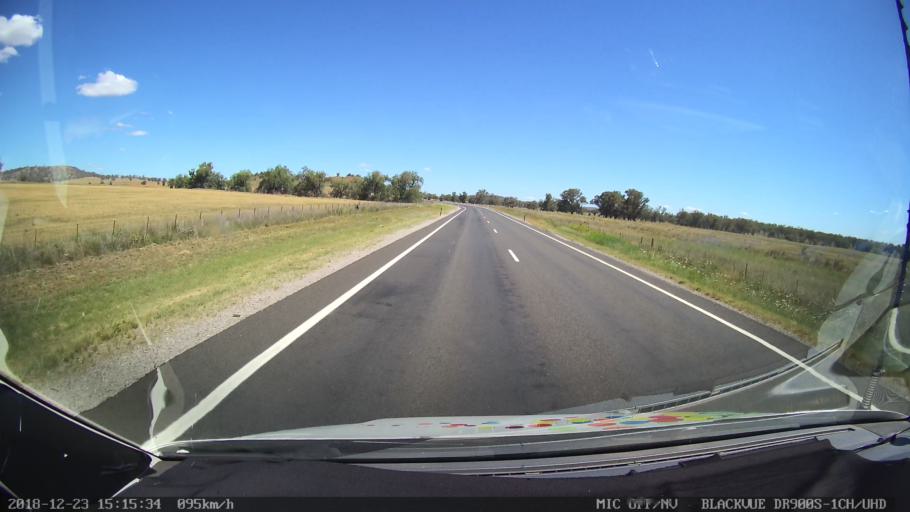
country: AU
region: New South Wales
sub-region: Tamworth Municipality
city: Manilla
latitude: -30.7877
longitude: 150.7434
